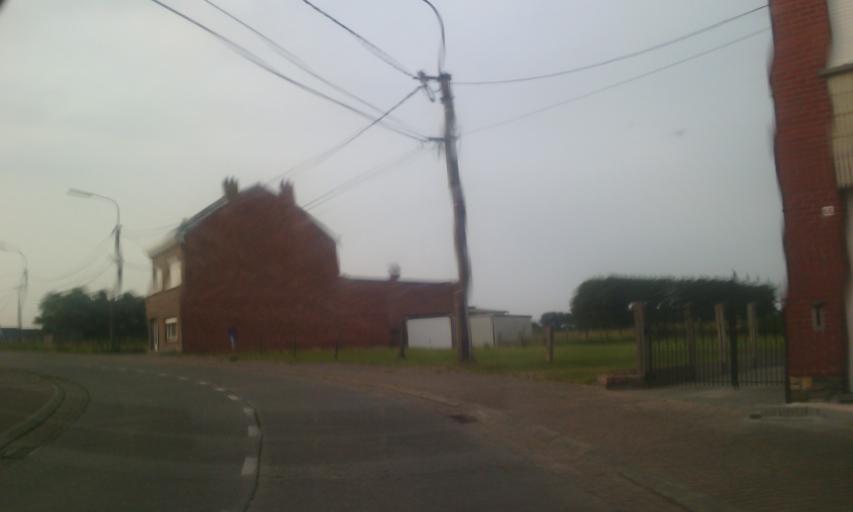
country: BE
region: Flanders
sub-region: Provincie Oost-Vlaanderen
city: Lede
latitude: 50.9764
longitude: 3.9574
